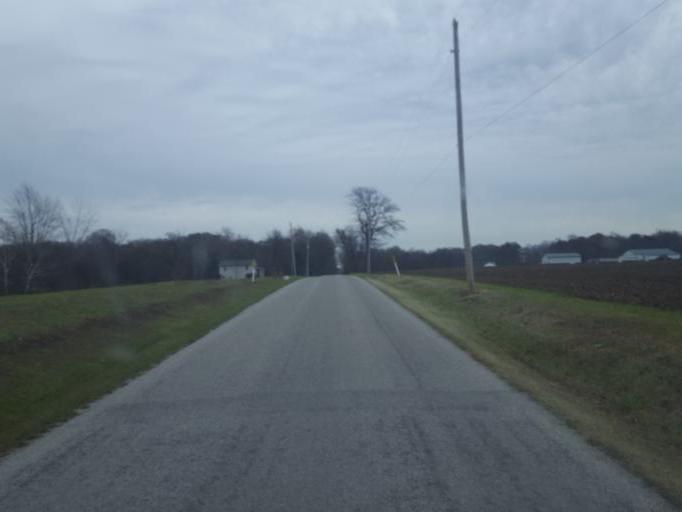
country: US
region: Ohio
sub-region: Morrow County
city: Mount Gilead
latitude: 40.5890
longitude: -82.8405
